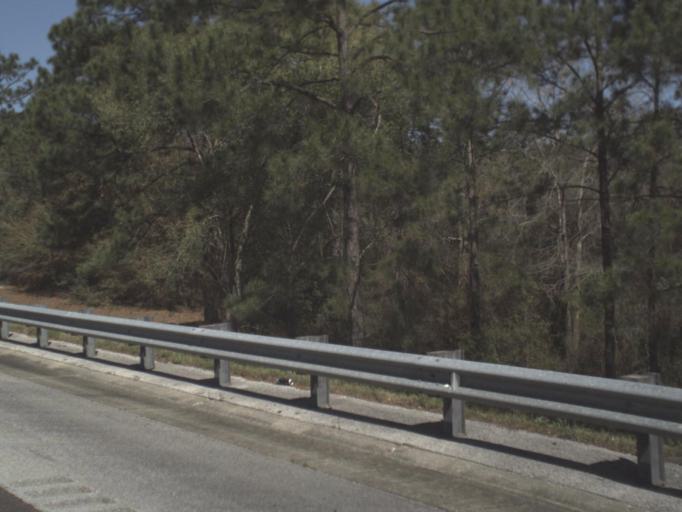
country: US
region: Florida
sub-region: Walton County
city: DeFuniak Springs
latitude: 30.7239
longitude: -86.1956
